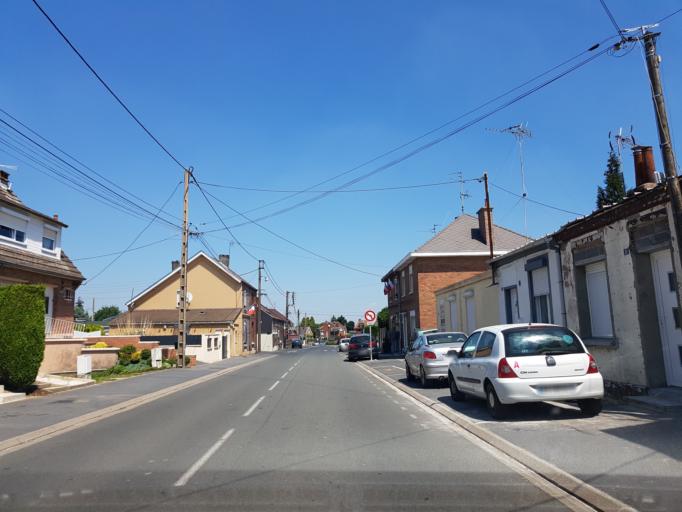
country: FR
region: Nord-Pas-de-Calais
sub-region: Departement du Nord
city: Neuville-sur-Escaut
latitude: 50.2962
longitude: 3.3566
